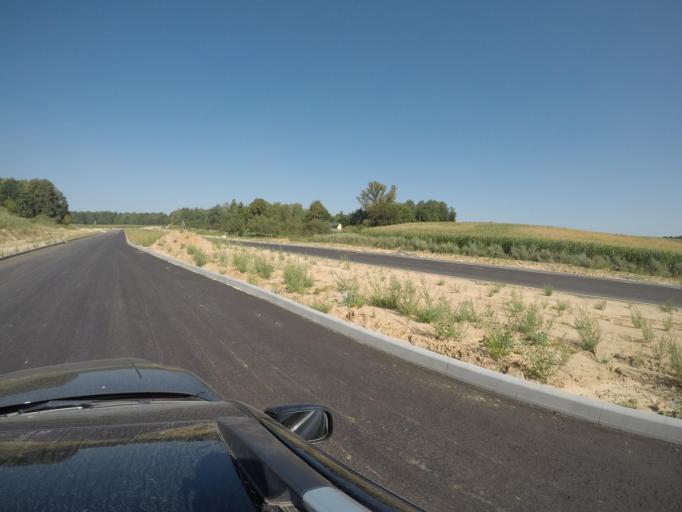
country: BY
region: Grodnenskaya
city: Hrodna
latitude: 53.7255
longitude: 23.8804
